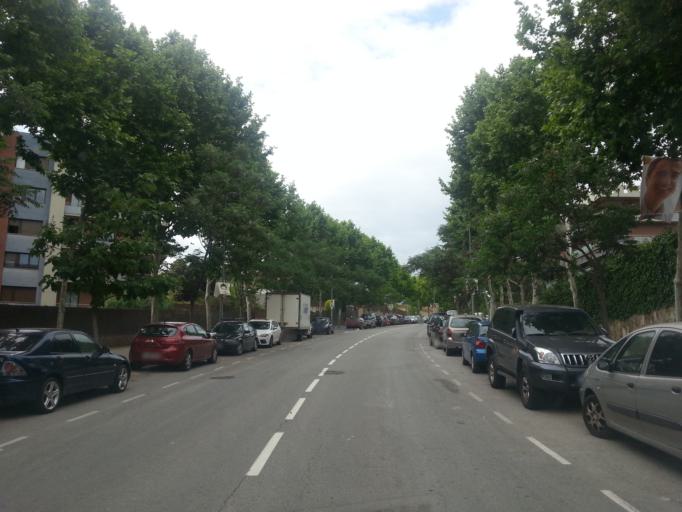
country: ES
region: Catalonia
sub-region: Provincia de Barcelona
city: Molins de Rei
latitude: 41.4170
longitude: 2.0227
